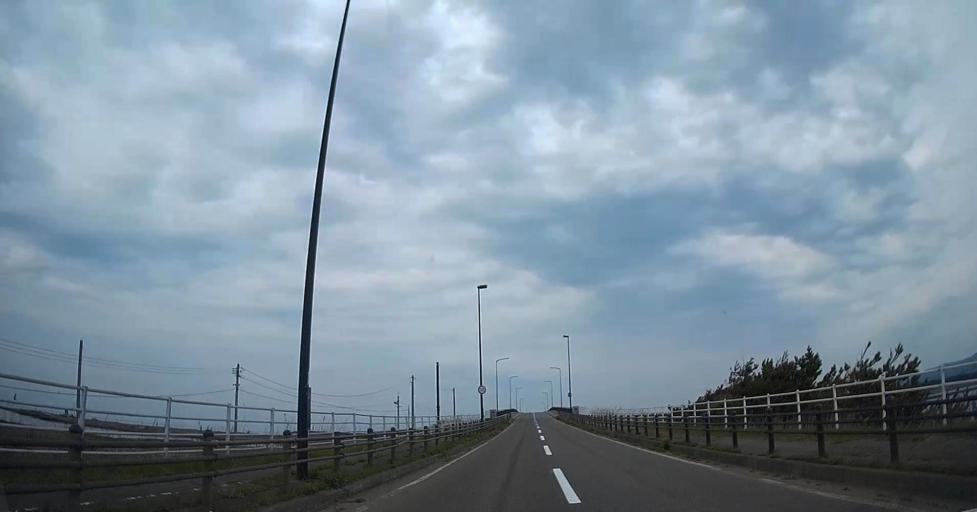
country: JP
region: Aomori
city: Shimokizukuri
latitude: 41.0373
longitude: 140.3277
